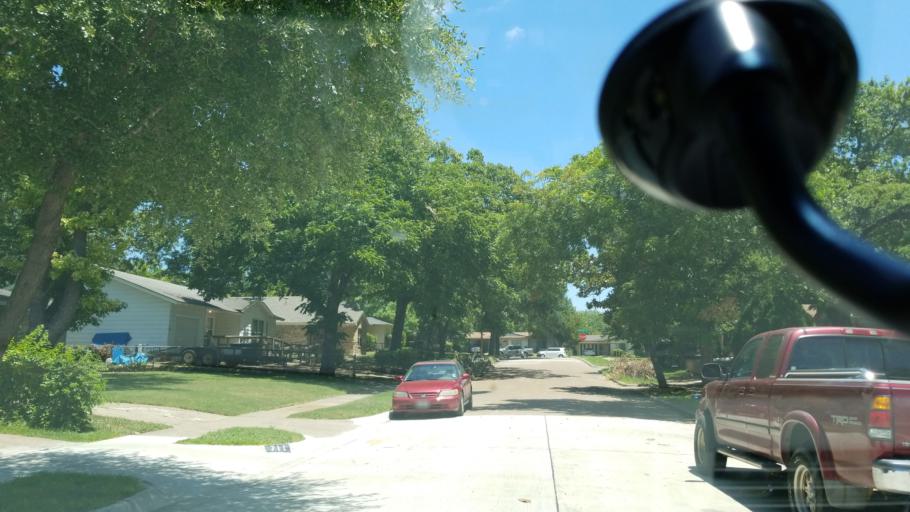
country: US
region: Texas
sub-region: Dallas County
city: Cockrell Hill
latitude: 32.6885
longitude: -96.8141
